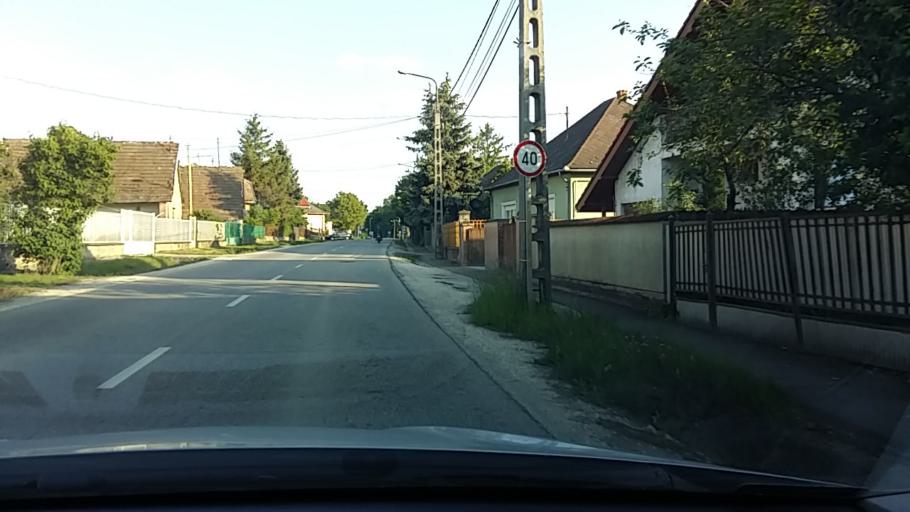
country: HU
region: Pest
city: Orbottyan
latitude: 47.7123
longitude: 19.2348
